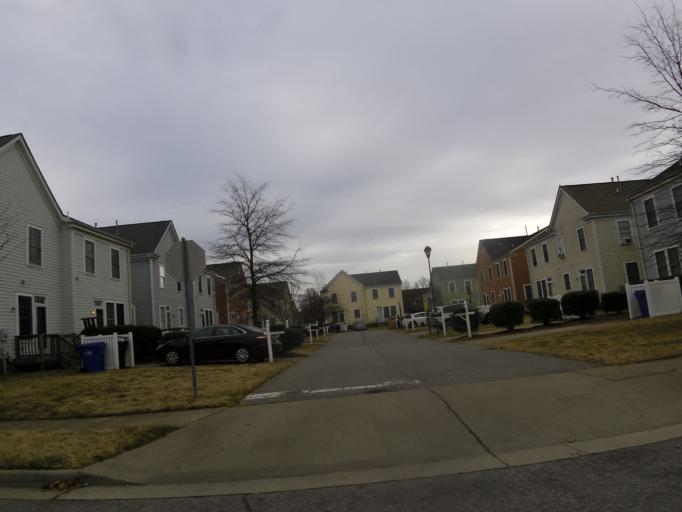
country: US
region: Virginia
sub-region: City of Portsmouth
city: Portsmouth
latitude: 36.8332
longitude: -76.3139
